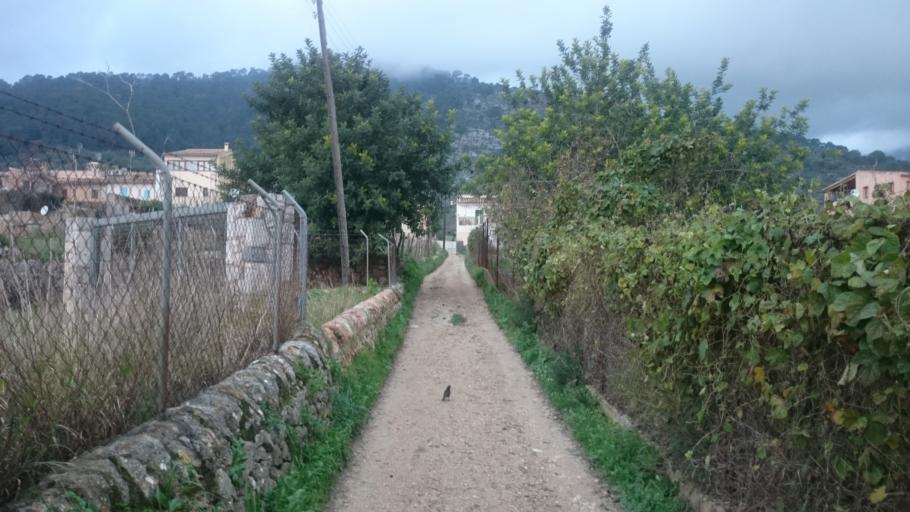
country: ES
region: Balearic Islands
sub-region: Illes Balears
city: Alaro
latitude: 39.7086
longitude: 2.7945
